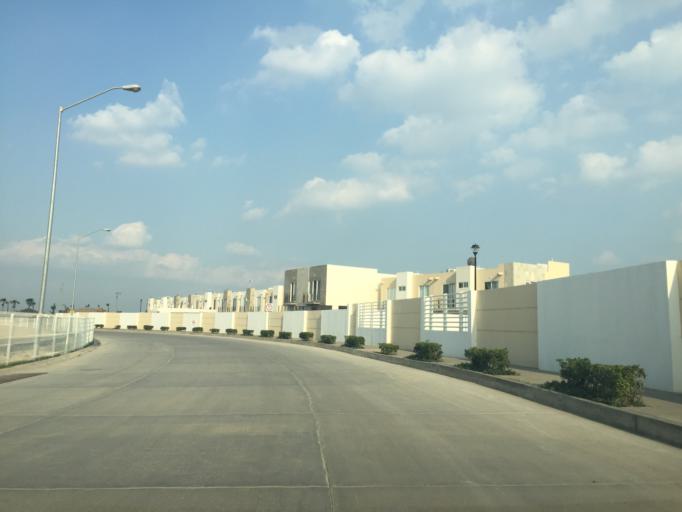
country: MX
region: Nuevo Leon
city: Apodaca
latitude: 25.7678
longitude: -100.2096
